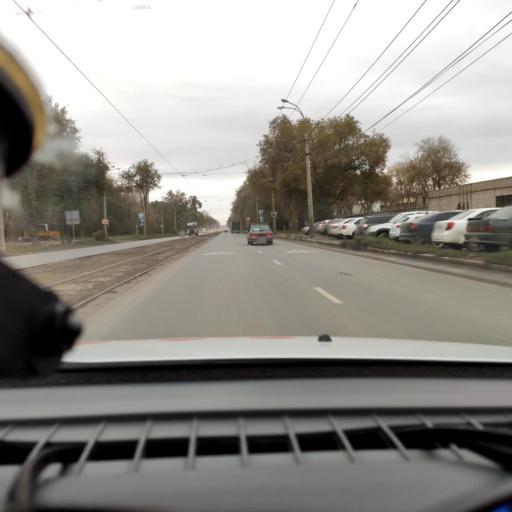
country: RU
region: Samara
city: Smyshlyayevka
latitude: 53.2022
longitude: 50.2831
